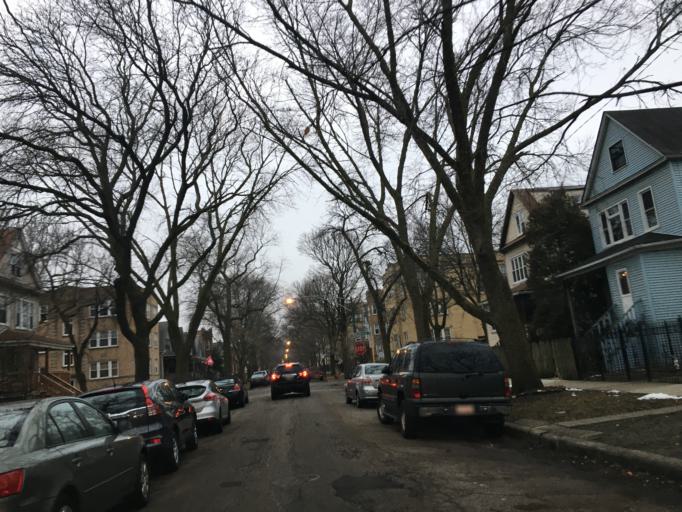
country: US
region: Illinois
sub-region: Cook County
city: Lincolnwood
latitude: 41.9636
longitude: -87.7157
